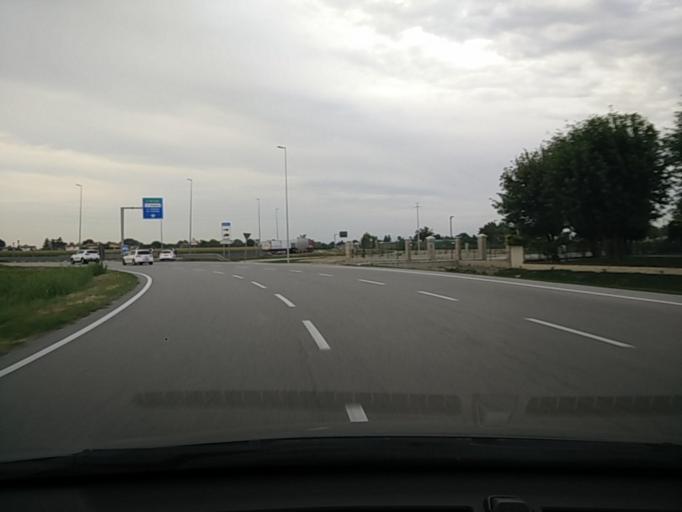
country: IT
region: Veneto
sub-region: Provincia di Venezia
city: Musile di Piave
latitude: 45.5814
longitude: 12.5600
